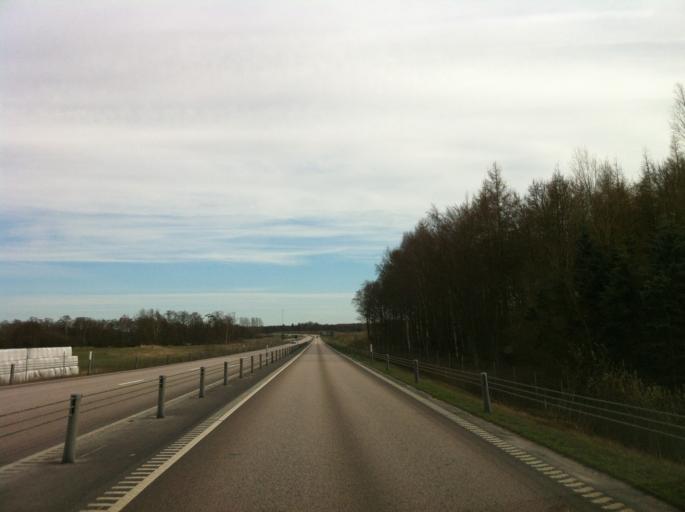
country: SE
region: Skane
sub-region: Helsingborg
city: Helsingborg
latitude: 56.1047
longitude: 12.6609
